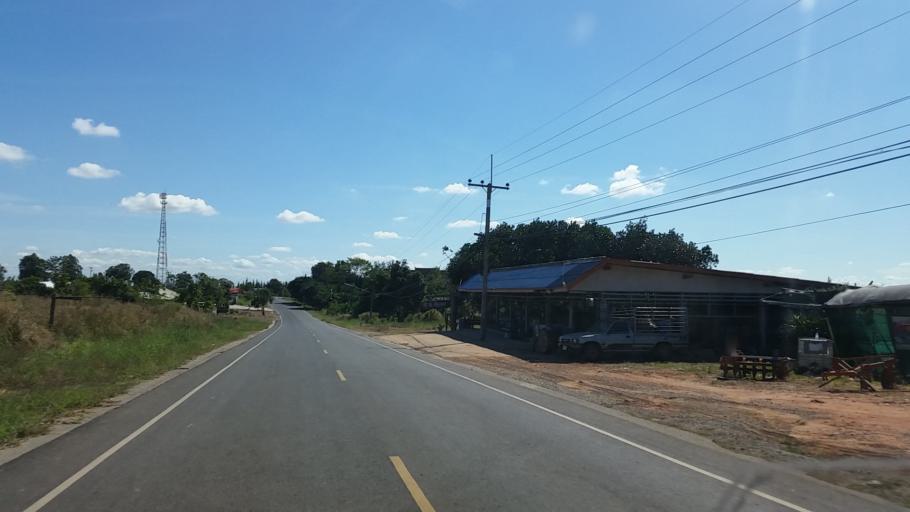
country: TH
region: Chaiyaphum
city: Sap Yai
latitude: 15.6046
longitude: 101.4058
